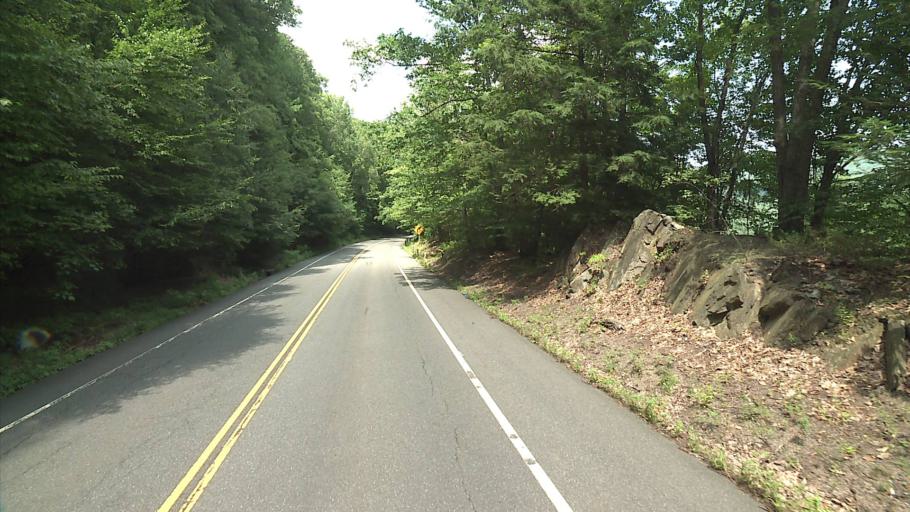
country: US
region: Massachusetts
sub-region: Hampden County
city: Granville
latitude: 42.0267
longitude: -72.9427
